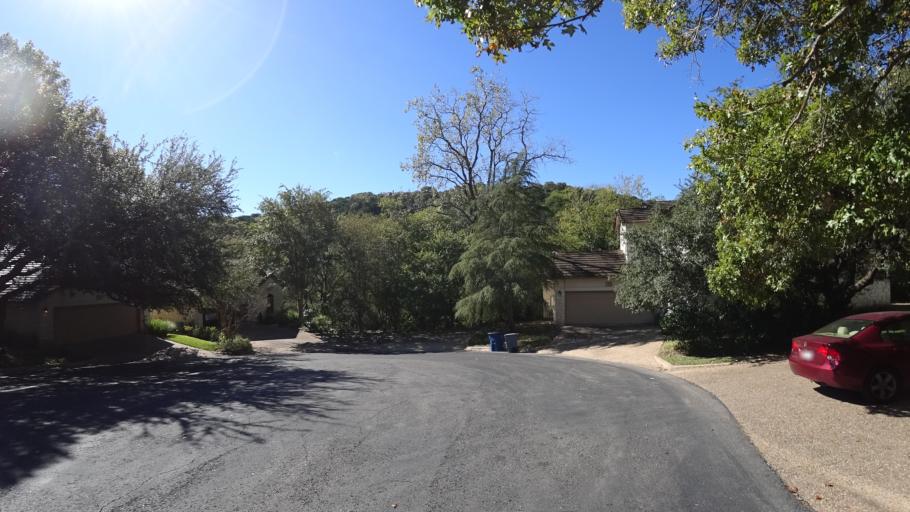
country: US
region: Texas
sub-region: Travis County
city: West Lake Hills
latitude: 30.3588
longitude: -97.7791
